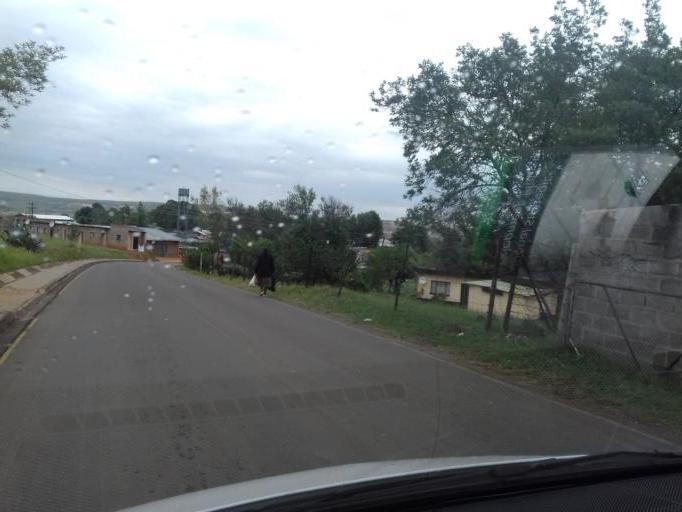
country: LS
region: Berea
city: Teyateyaneng
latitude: -29.1035
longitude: 27.9582
